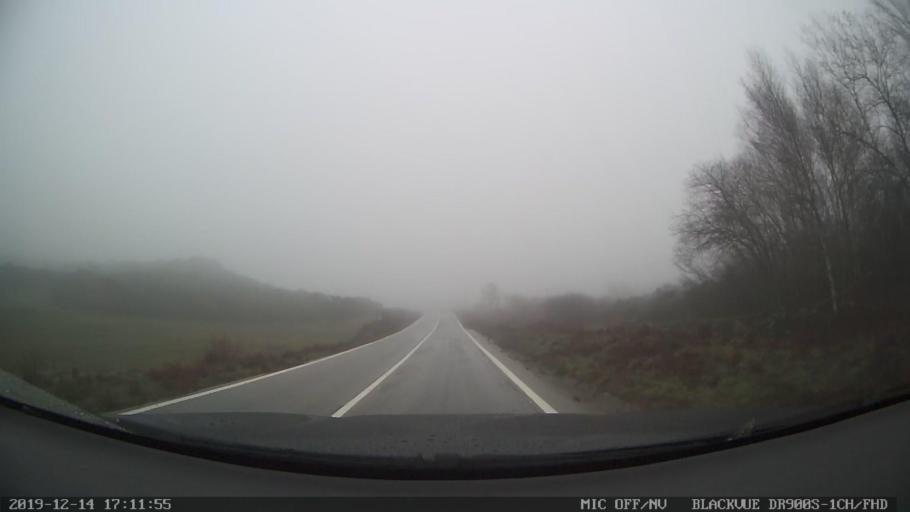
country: PT
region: Vila Real
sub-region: Vila Pouca de Aguiar
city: Vila Pouca de Aguiar
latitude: 41.4889
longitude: -7.6195
